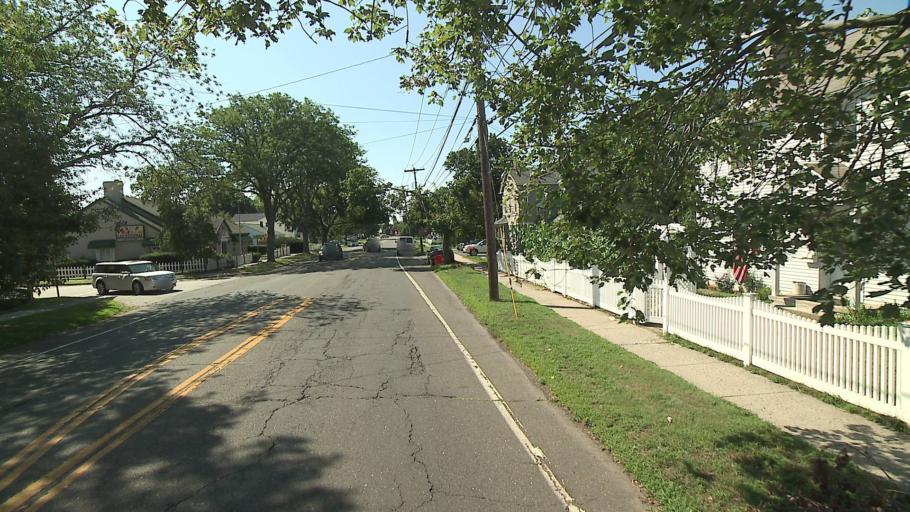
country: US
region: Connecticut
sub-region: Fairfield County
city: Stratford
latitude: 41.1789
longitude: -73.1303
